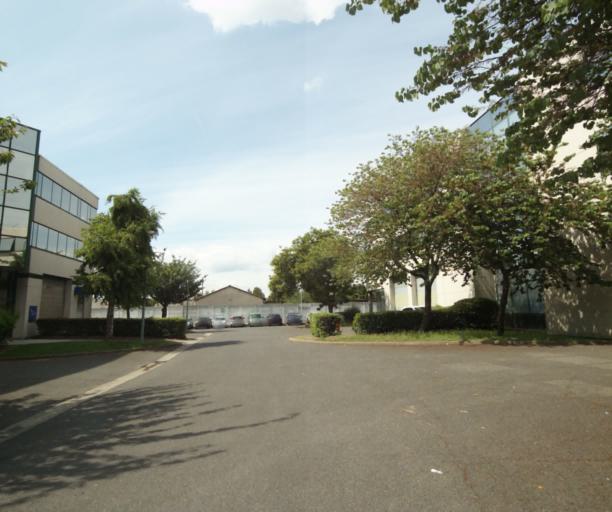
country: FR
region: Ile-de-France
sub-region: Departement des Hauts-de-Seine
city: Colombes
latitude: 48.9336
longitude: 2.2499
